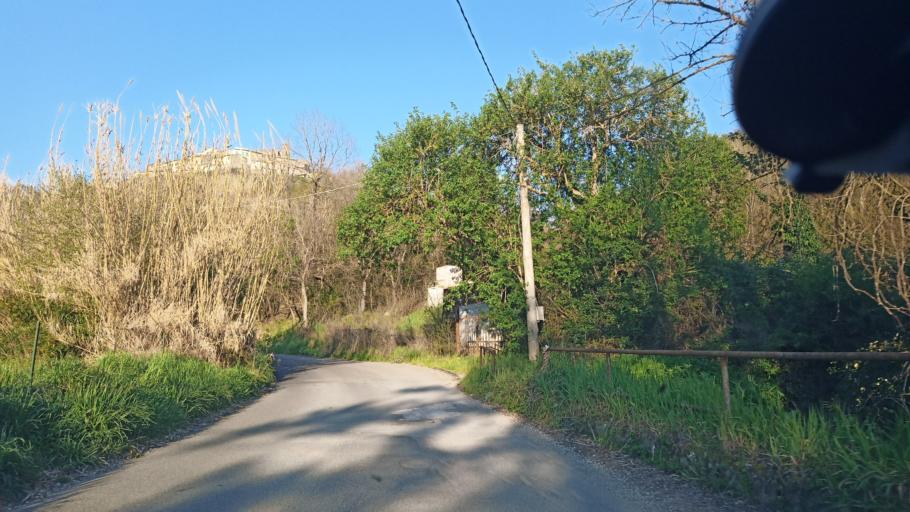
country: IT
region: Latium
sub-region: Provincia di Rieti
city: Poggio Mirteto
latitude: 42.2621
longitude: 12.6744
